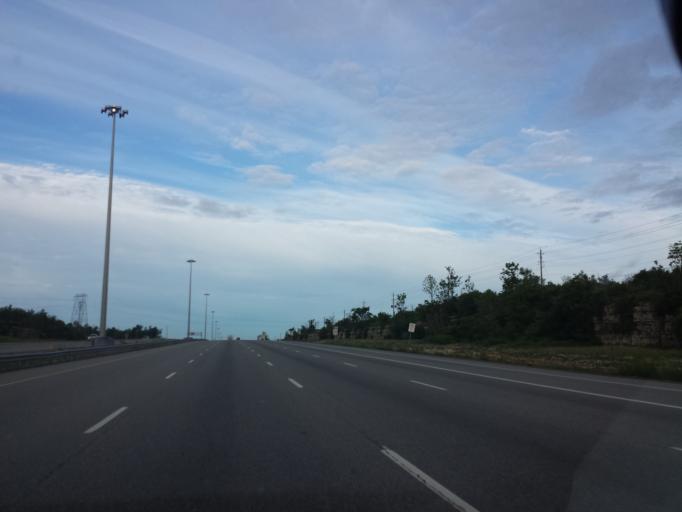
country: CA
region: Ontario
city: Bells Corners
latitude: 45.3295
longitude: -75.8637
